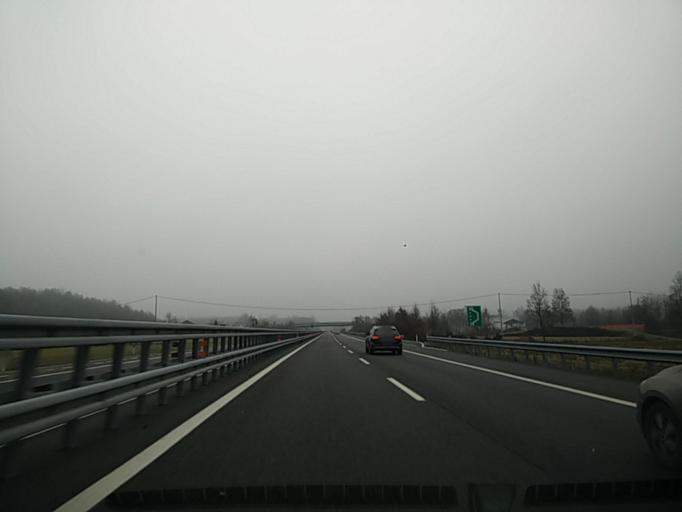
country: IT
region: Piedmont
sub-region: Provincia di Asti
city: Villafranca d'Asti
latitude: 44.9107
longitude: 8.0459
